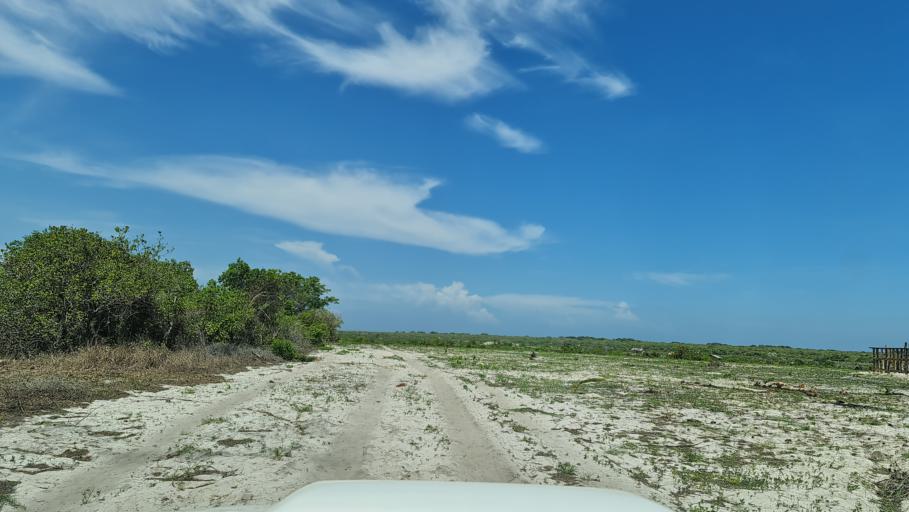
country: MZ
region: Nampula
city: Ilha de Mocambique
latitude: -15.1957
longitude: 40.6176
